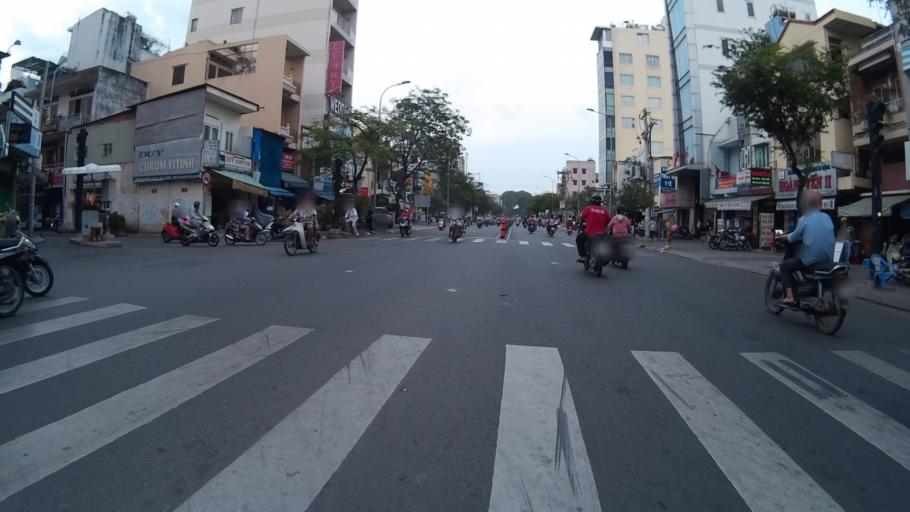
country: VN
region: Ho Chi Minh City
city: Quan Binh Thanh
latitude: 10.7955
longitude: 106.6962
